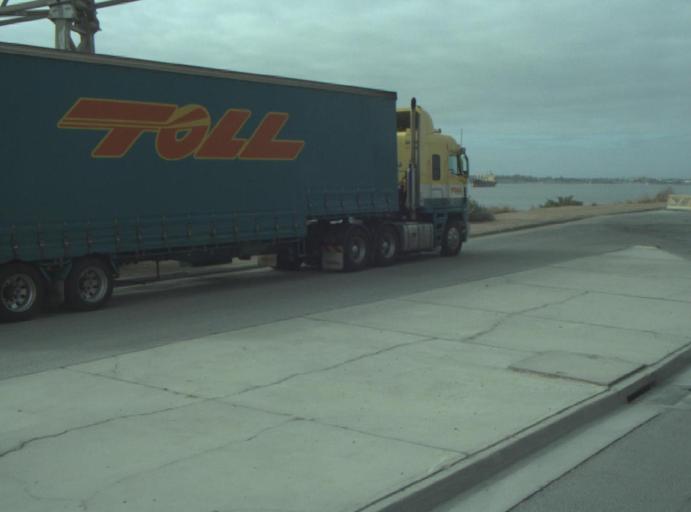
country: AU
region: Victoria
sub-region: Greater Geelong
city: Bell Park
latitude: -38.0971
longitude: 144.3800
